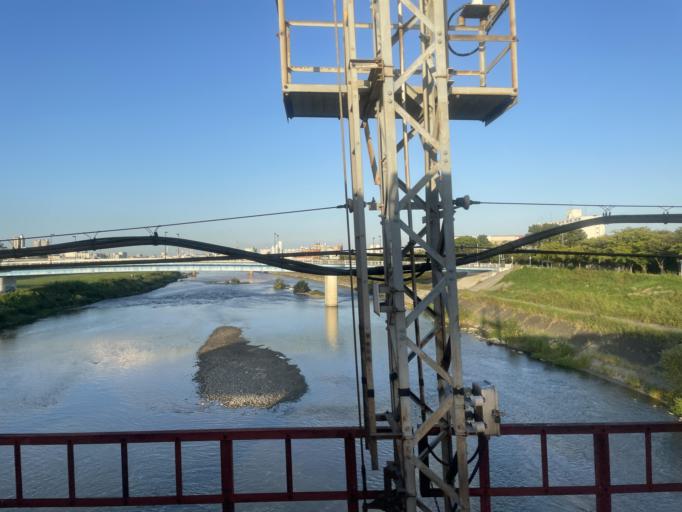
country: JP
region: Osaka
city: Matsubara
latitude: 34.5982
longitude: 135.5323
